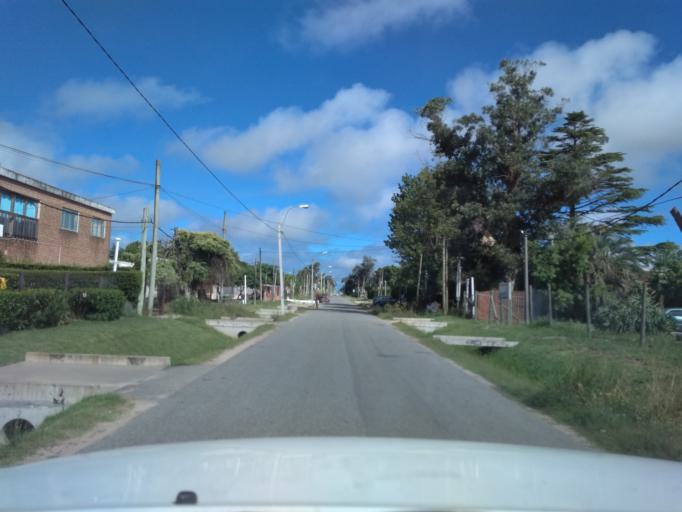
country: UY
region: Canelones
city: Barra de Carrasco
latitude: -34.8322
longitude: -55.9746
